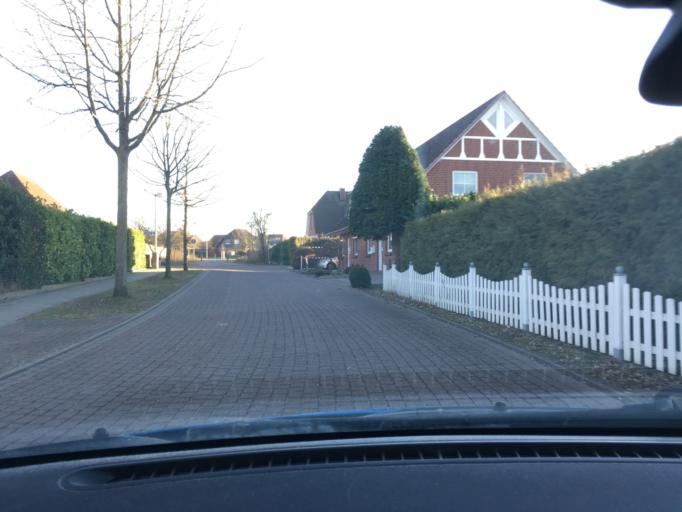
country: DE
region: Lower Saxony
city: Wendisch Evern
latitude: 53.2359
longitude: 10.4500
